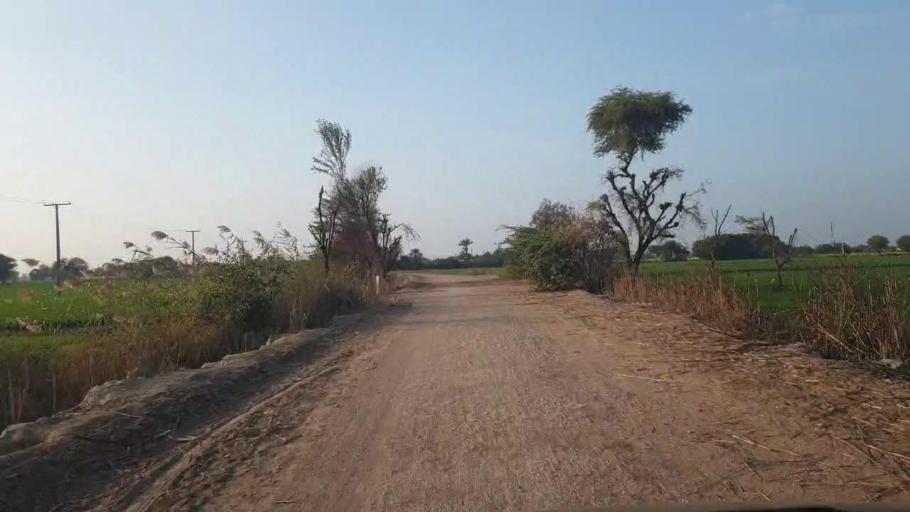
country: PK
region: Sindh
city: Berani
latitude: 25.8597
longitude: 68.7367
